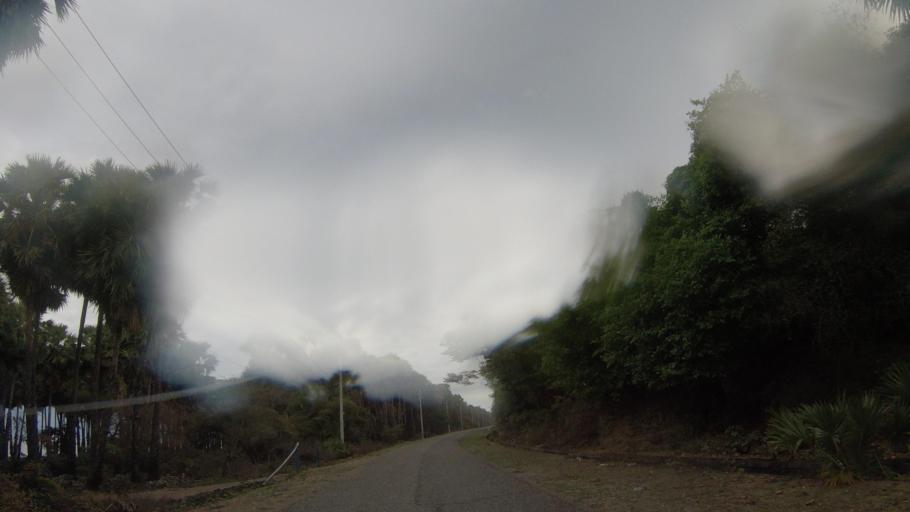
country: TL
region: Lautem
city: Lospalos
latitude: -8.3429
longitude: 126.9290
